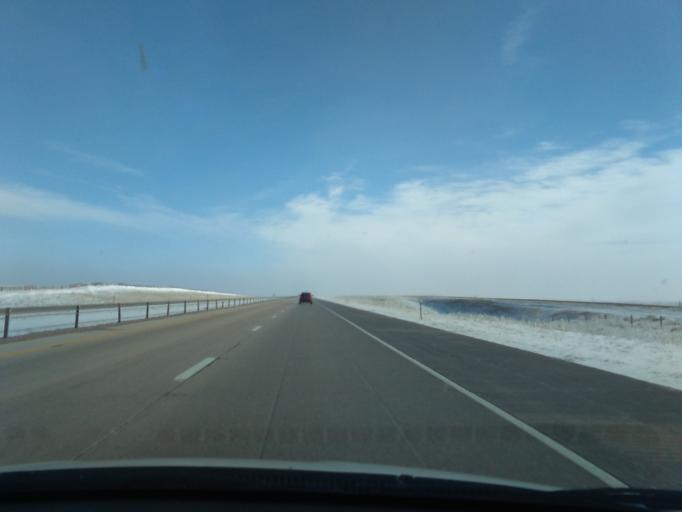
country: US
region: Wyoming
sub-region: Laramie County
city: Pine Bluffs
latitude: 41.1587
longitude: -104.3096
